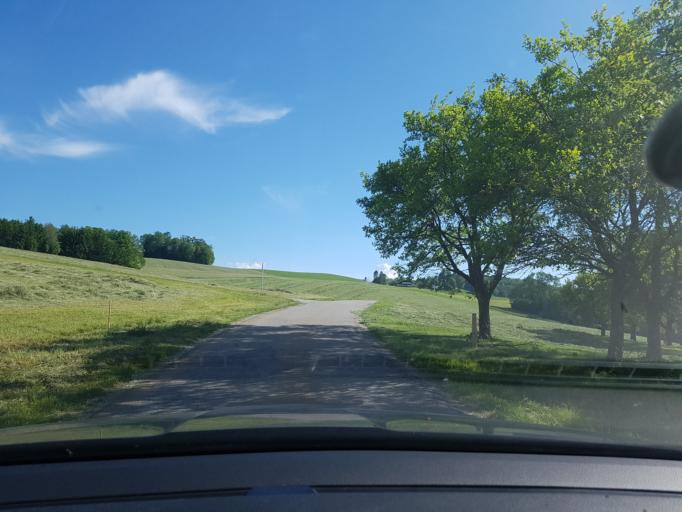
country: AT
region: Salzburg
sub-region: Politischer Bezirk Salzburg-Umgebung
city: Schleedorf
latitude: 47.9874
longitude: 13.1529
